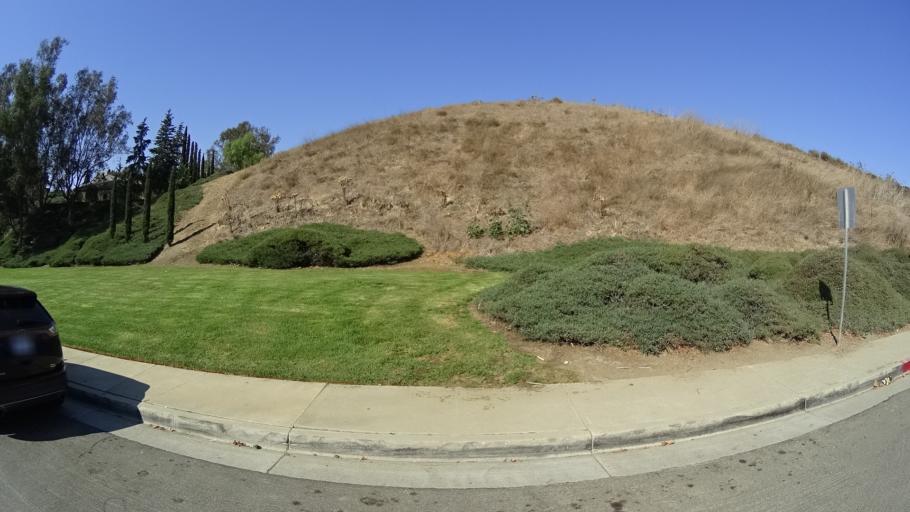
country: US
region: California
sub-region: Orange County
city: San Juan Capistrano
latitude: 33.4786
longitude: -117.6285
